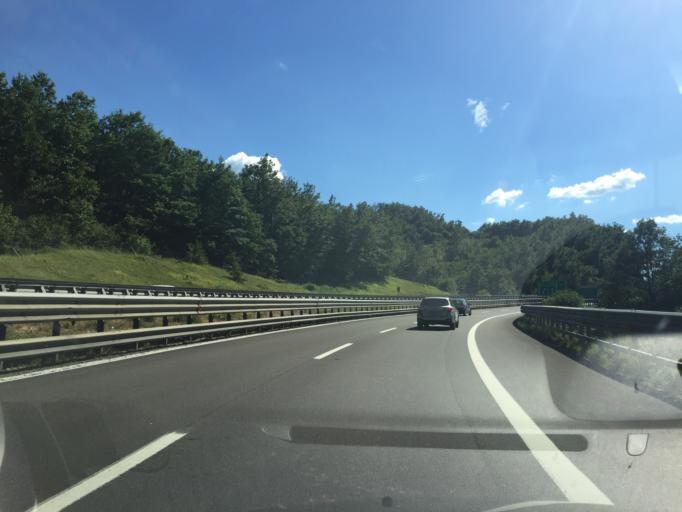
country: IT
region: Emilia-Romagna
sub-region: Provincia di Parma
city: Stazione Valmozzola
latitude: 44.5670
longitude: 9.9522
